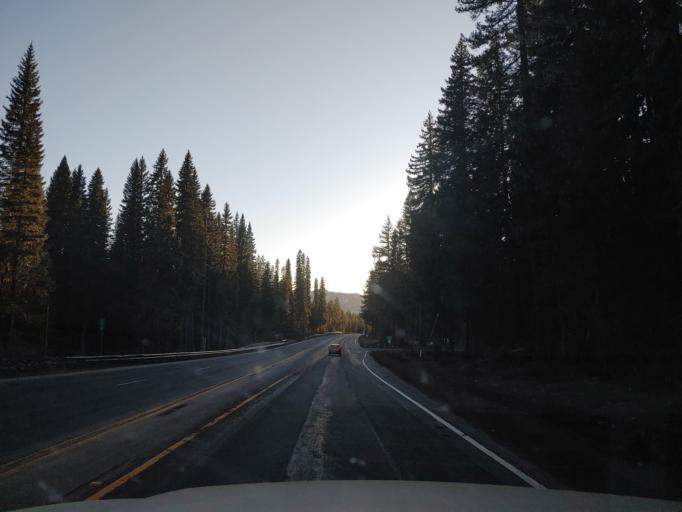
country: US
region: Oregon
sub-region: Lane County
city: Oakridge
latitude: 43.6179
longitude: -122.0812
